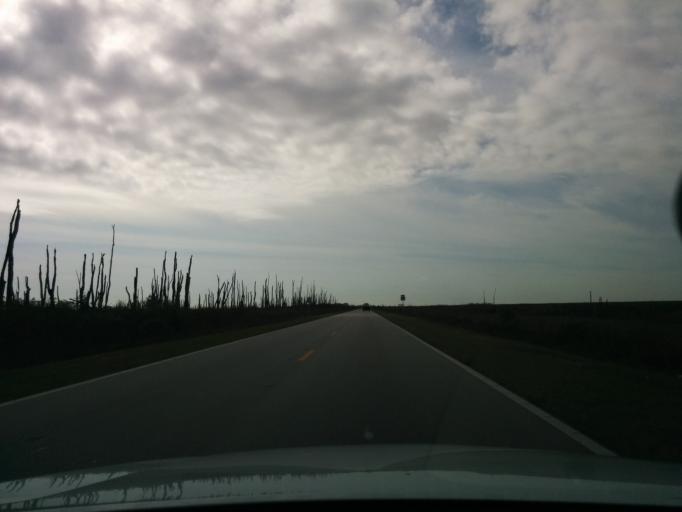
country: US
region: Florida
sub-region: Miami-Dade County
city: Tamiami
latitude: 25.8253
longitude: -80.4827
